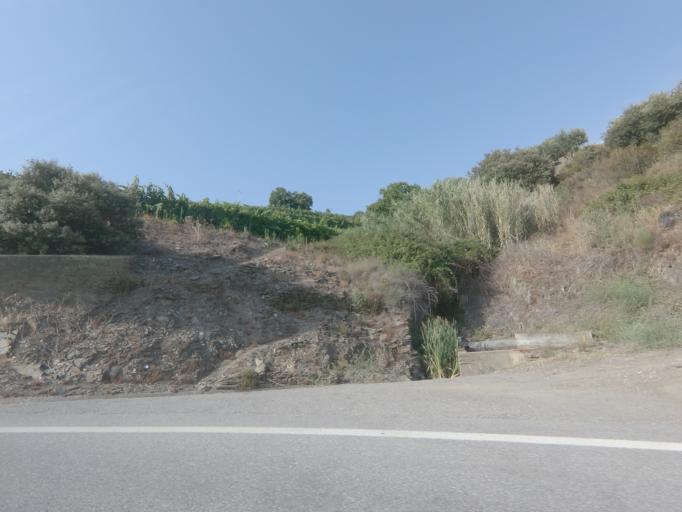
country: PT
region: Viseu
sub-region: Tabuaco
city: Tabuaco
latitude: 41.1395
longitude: -7.5378
